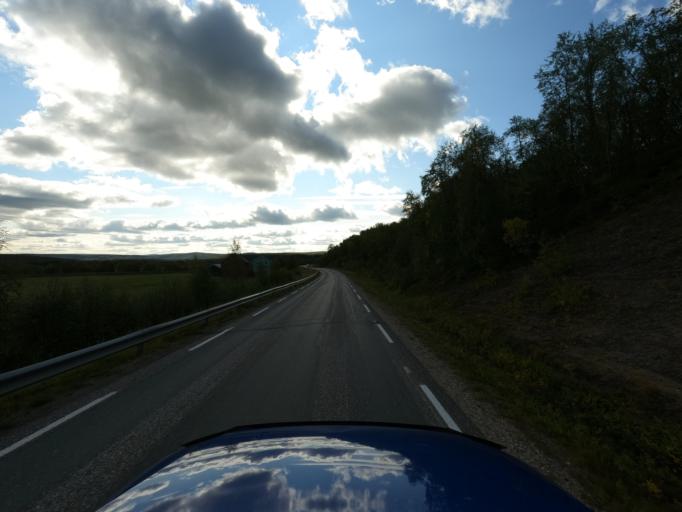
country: NO
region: Finnmark Fylke
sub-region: Karasjok
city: Karasjohka
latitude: 69.4258
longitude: 25.7938
